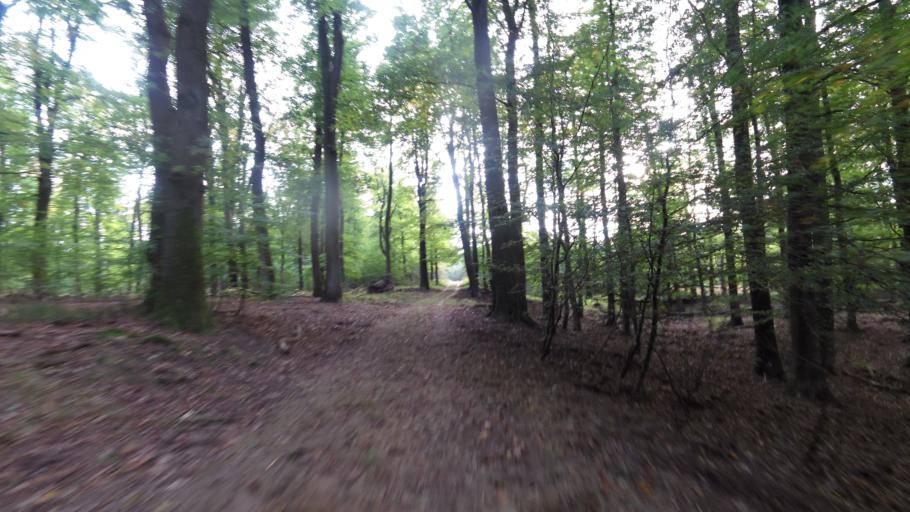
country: NL
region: Gelderland
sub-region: Gemeente Epe
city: Vaassen
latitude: 52.3216
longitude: 5.8714
